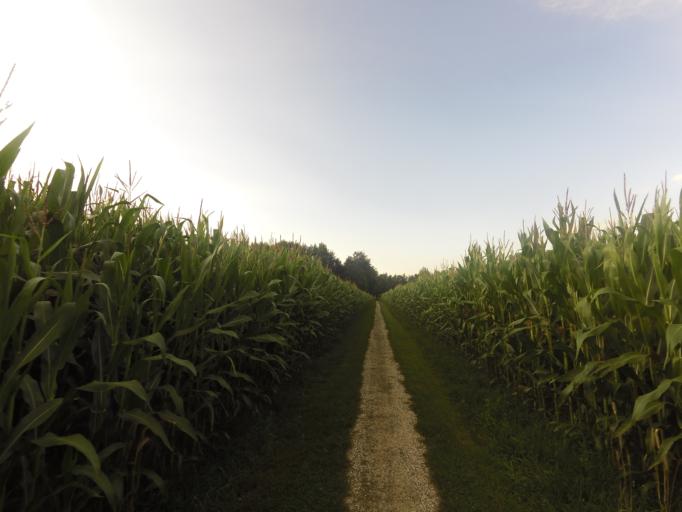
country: NL
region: Gelderland
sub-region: Oude IJsselstreek
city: Varsseveld
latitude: 51.8981
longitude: 6.4638
